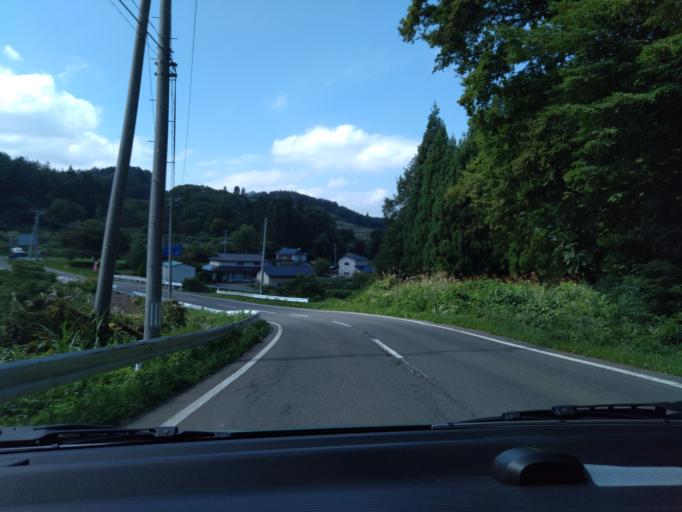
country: JP
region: Iwate
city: Shizukuishi
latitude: 39.6454
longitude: 140.9951
